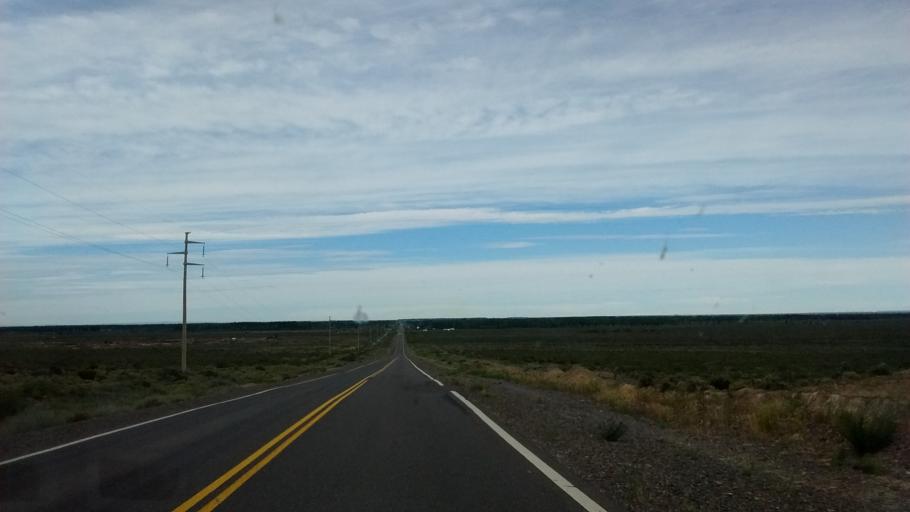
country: AR
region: Rio Negro
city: Contraalmirante Cordero
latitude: -38.6469
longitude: -68.1366
